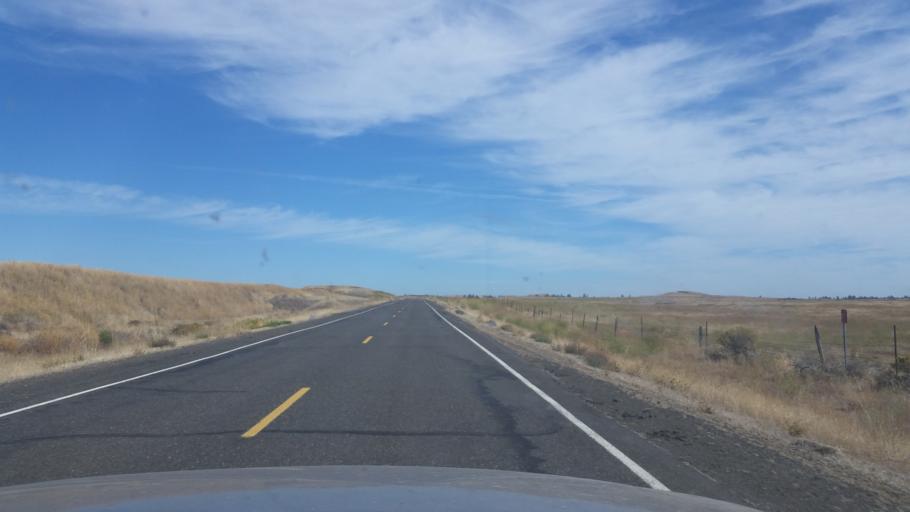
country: US
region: Washington
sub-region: Spokane County
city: Medical Lake
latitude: 47.3146
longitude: -117.9063
